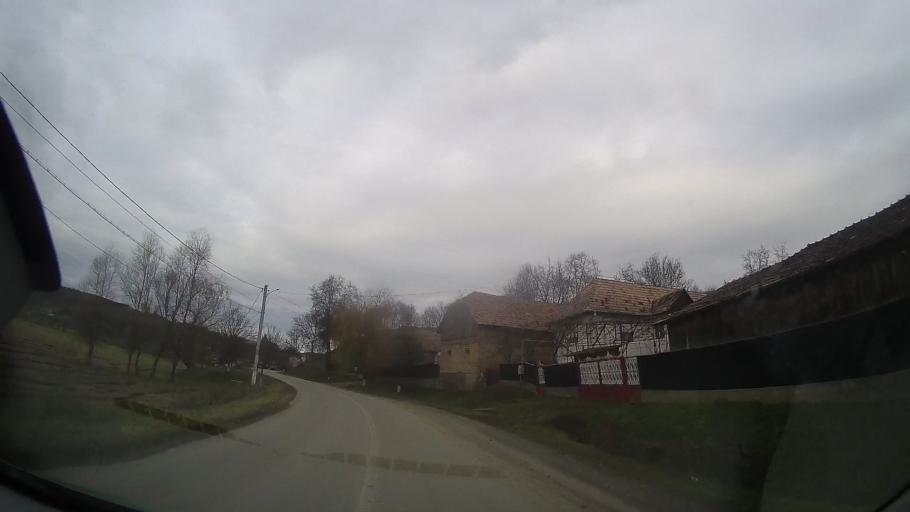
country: RO
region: Mures
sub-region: Comuna Faragau
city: Faragau
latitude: 46.7571
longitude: 24.5181
